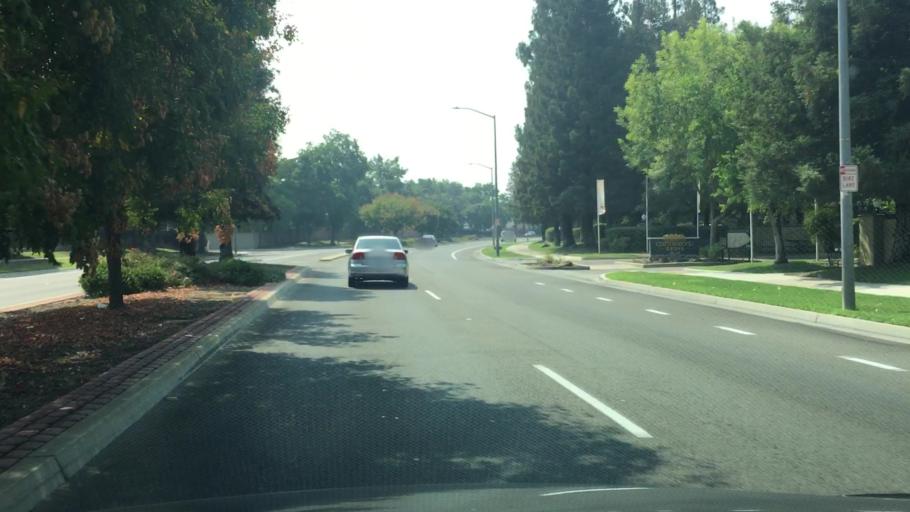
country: US
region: California
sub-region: Fresno County
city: Clovis
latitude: 36.8436
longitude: -119.7008
